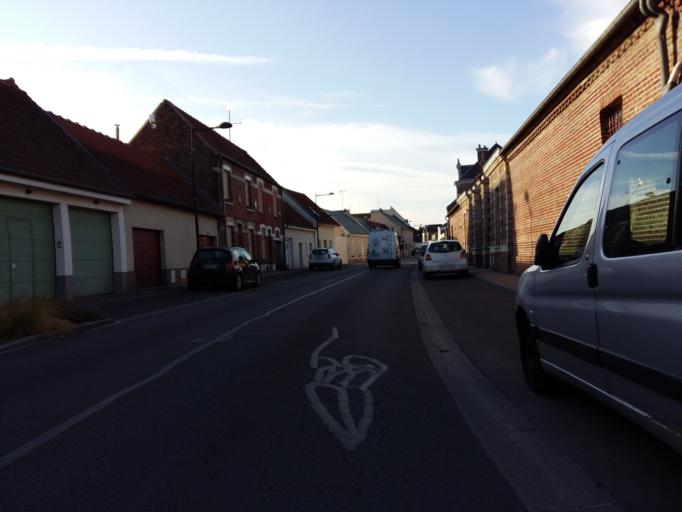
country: FR
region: Picardie
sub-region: Departement de la Somme
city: Camon
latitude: 49.8889
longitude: 2.3422
